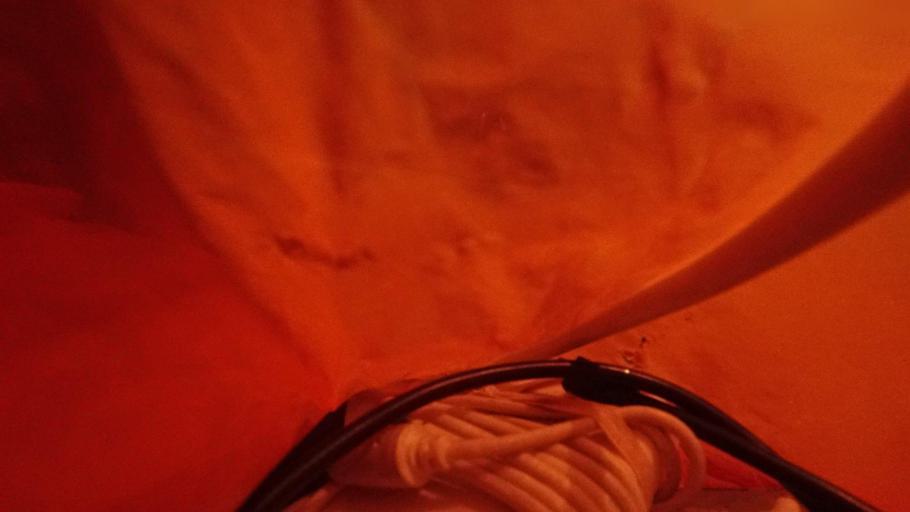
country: RU
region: Jewish Autonomous Oblast
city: Khingansk
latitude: 49.1651
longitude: 130.7965
